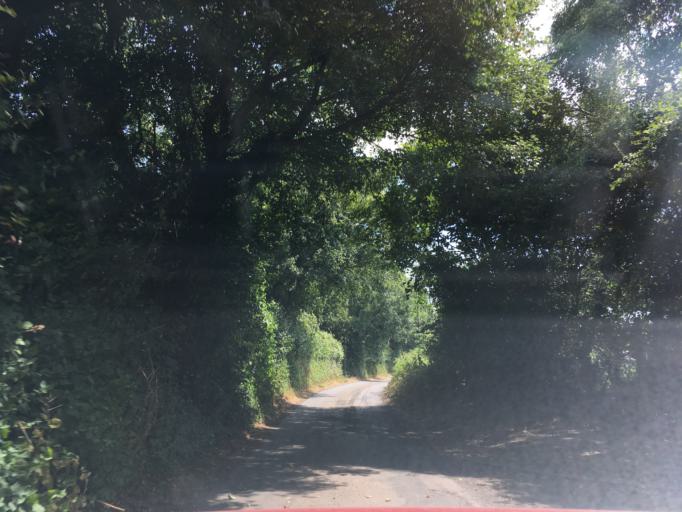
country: GB
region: Wales
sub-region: Monmouthshire
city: Magor
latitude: 51.6057
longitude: -2.8460
